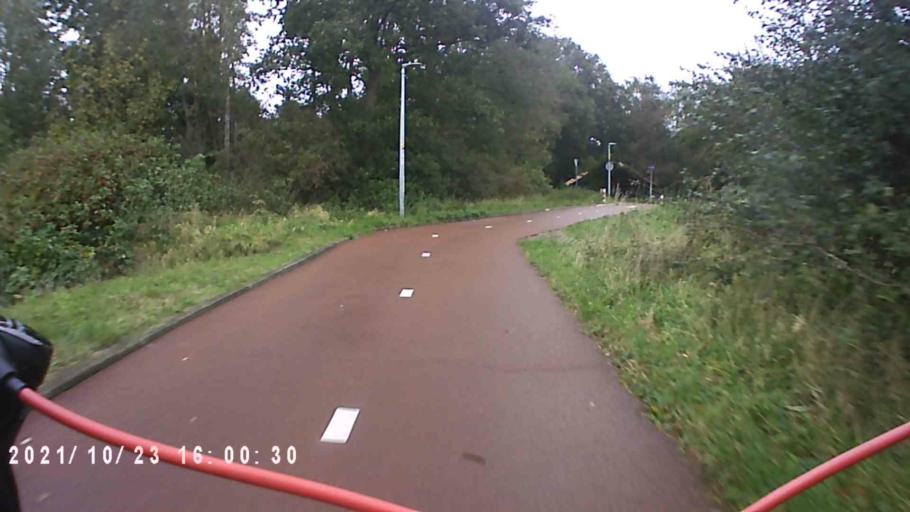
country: NL
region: North Holland
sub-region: Gemeente Alkmaar
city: Alkmaar
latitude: 52.6475
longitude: 4.7808
